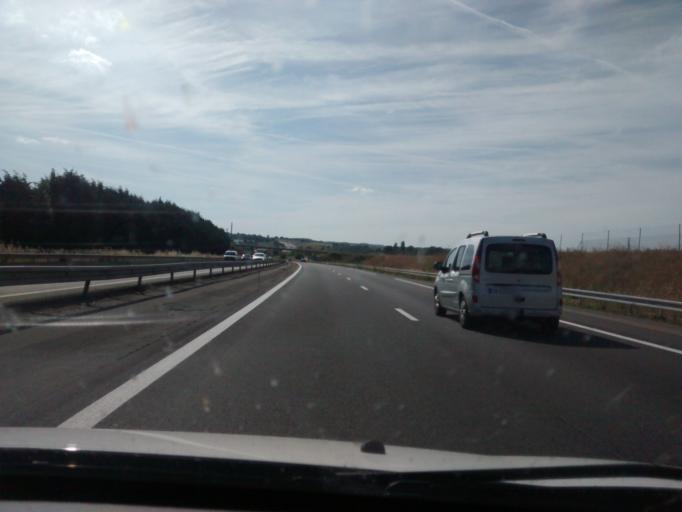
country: FR
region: Pays de la Loire
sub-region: Departement de la Mayenne
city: Saint-Jean-sur-Mayenne
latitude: 48.1108
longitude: -0.7530
